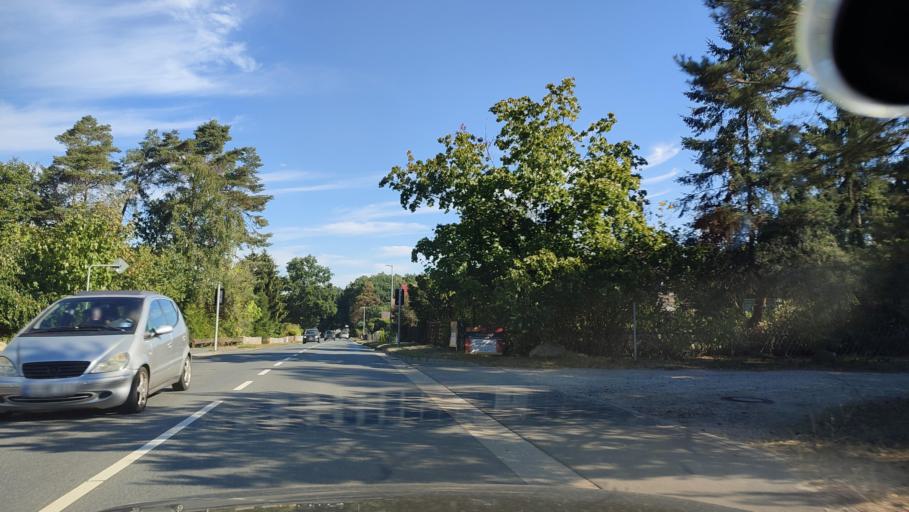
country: DE
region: Lower Saxony
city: Bomlitz
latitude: 52.8772
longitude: 9.6376
